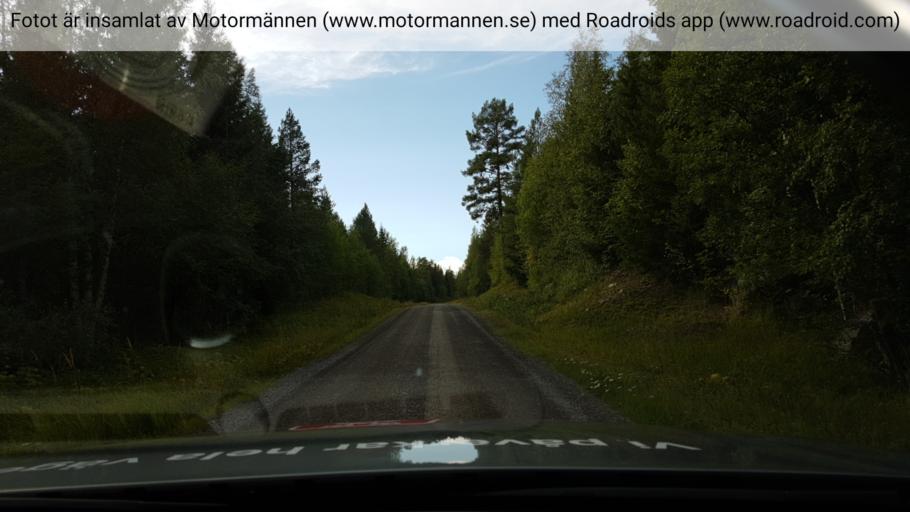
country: SE
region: Jaemtland
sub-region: OEstersunds Kommun
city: Lit
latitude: 63.3011
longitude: 15.3087
